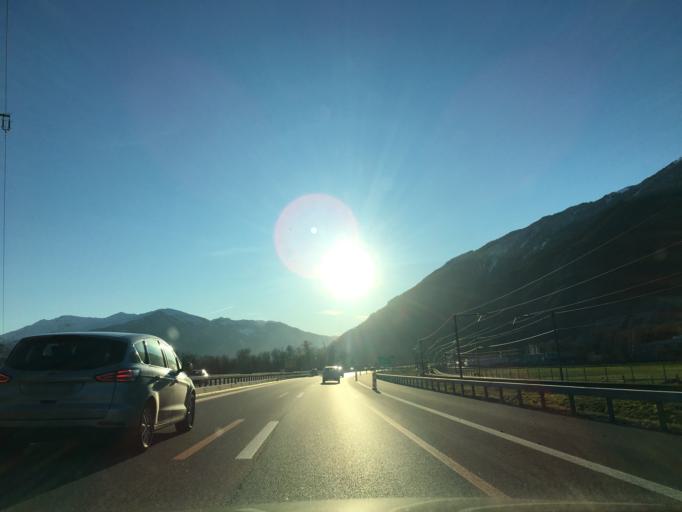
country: CH
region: Grisons
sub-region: Landquart District
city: Trimmis
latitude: 46.9125
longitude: 9.5585
